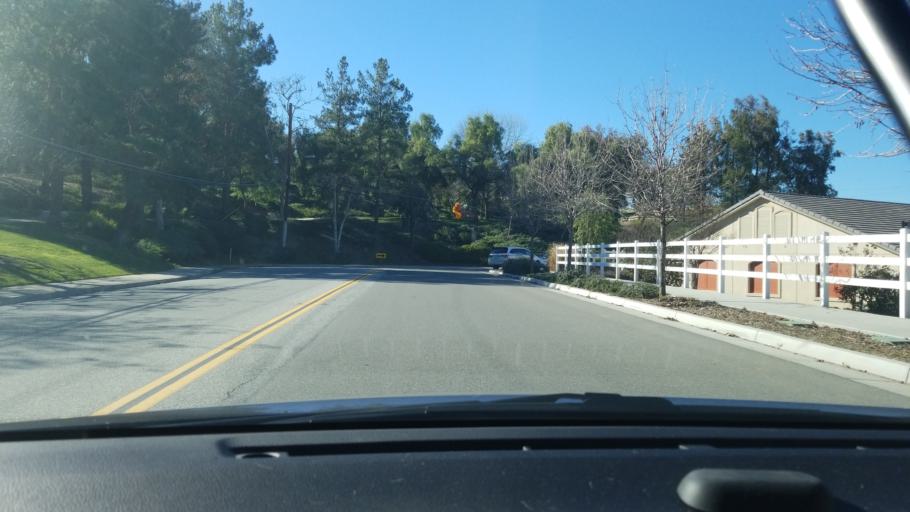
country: US
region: California
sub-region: Riverside County
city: Murrieta Hot Springs
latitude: 33.5403
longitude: -117.1096
